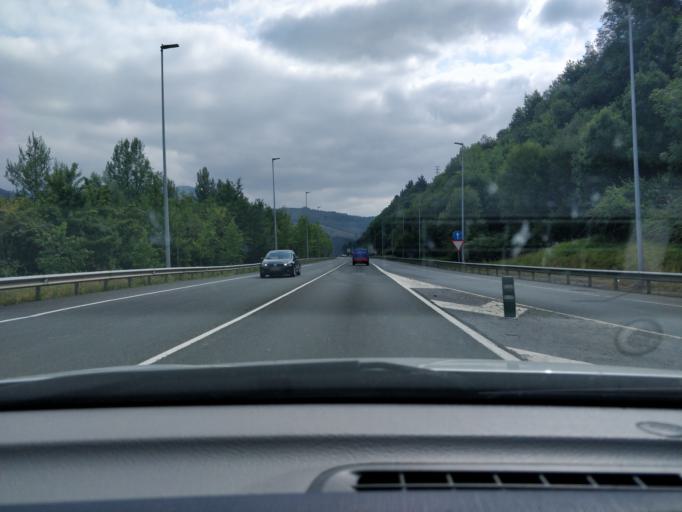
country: ES
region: Basque Country
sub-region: Bizkaia
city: Guenes
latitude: 43.2059
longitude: -3.1194
